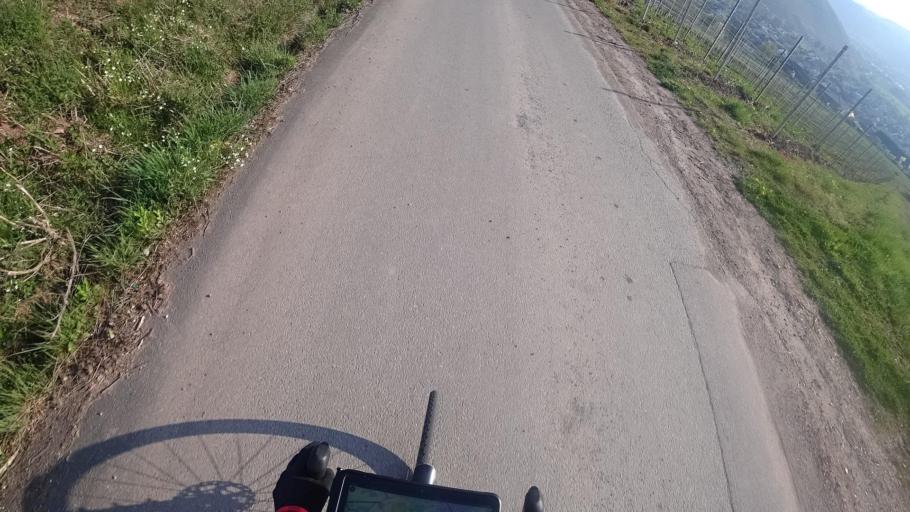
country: DE
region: Rheinland-Pfalz
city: Ayl
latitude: 49.6290
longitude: 6.5476
